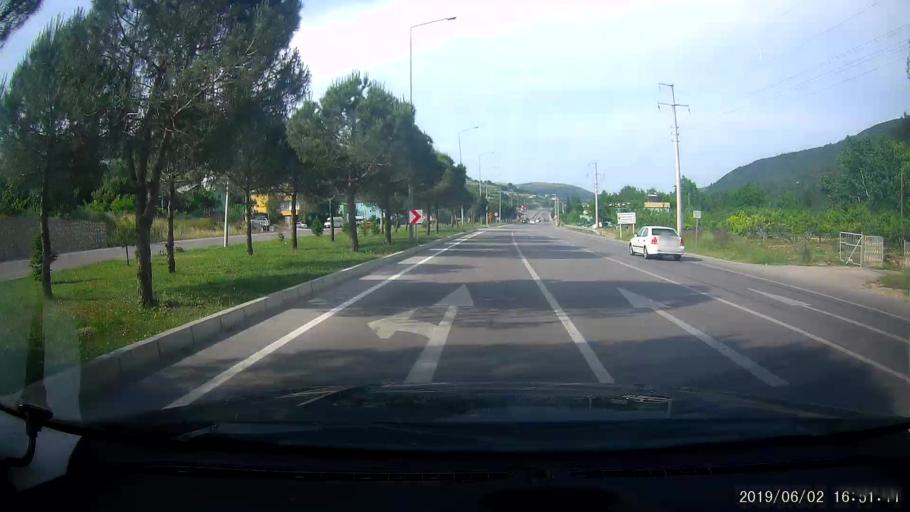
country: TR
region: Samsun
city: Taflan
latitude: 41.2699
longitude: 36.1789
